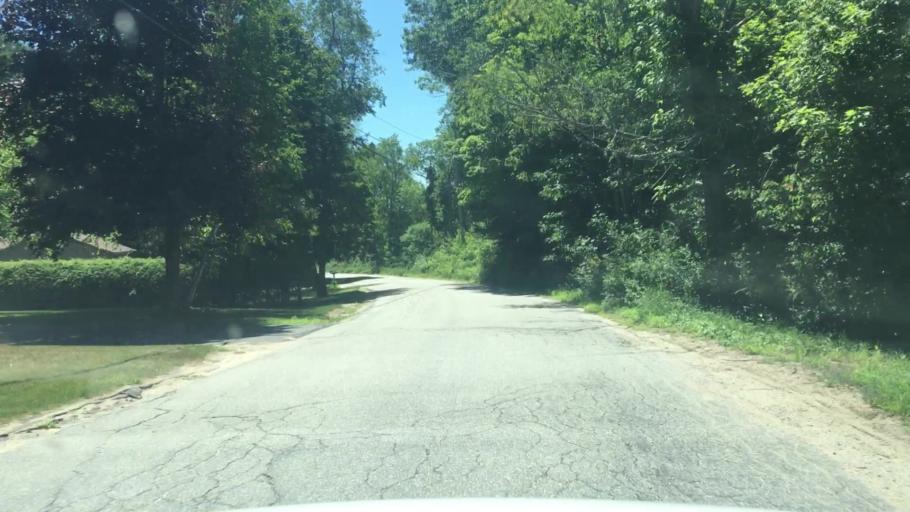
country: US
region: New Hampshire
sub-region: Merrimack County
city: Hopkinton
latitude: 43.2212
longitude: -71.6773
